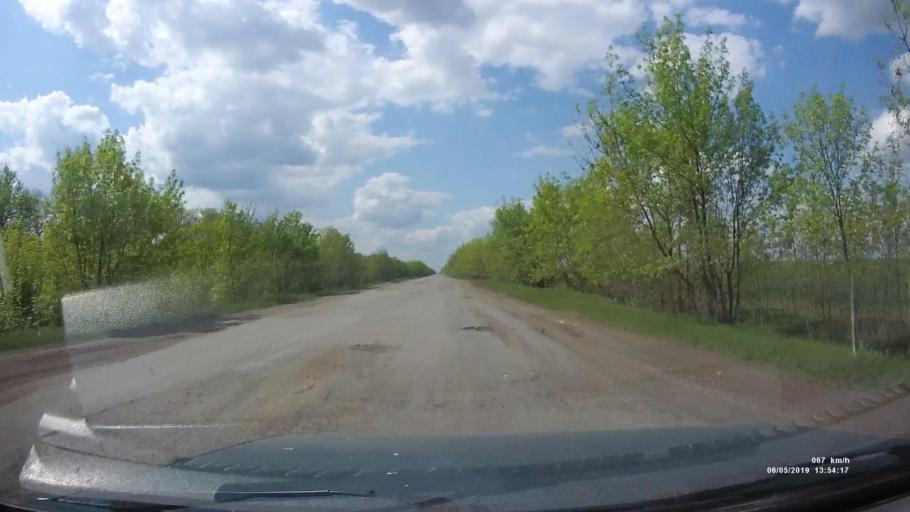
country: RU
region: Rostov
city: Melikhovskaya
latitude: 47.6736
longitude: 40.4494
